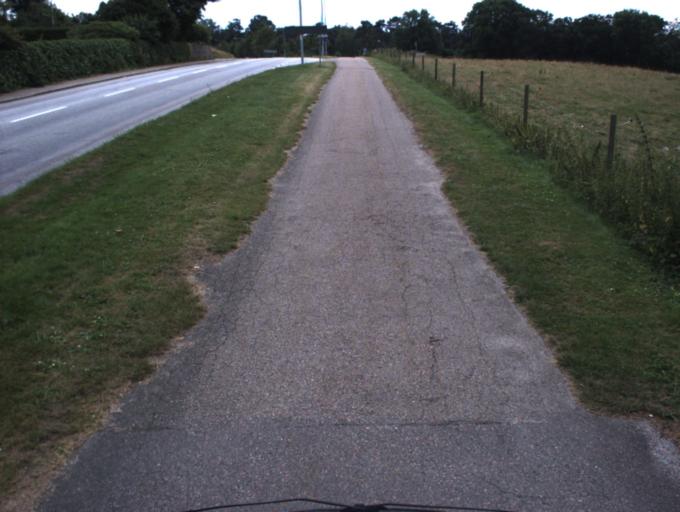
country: SE
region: Skane
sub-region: Helsingborg
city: Helsingborg
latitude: 56.0835
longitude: 12.6635
